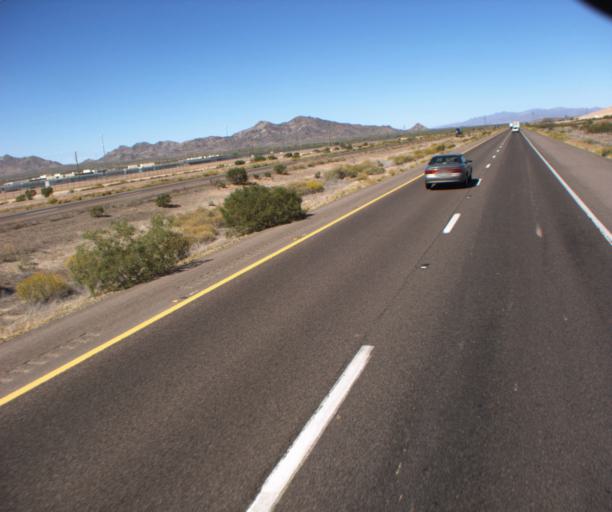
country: US
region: Arizona
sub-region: Maricopa County
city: Buckeye
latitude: 33.2086
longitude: -112.6460
